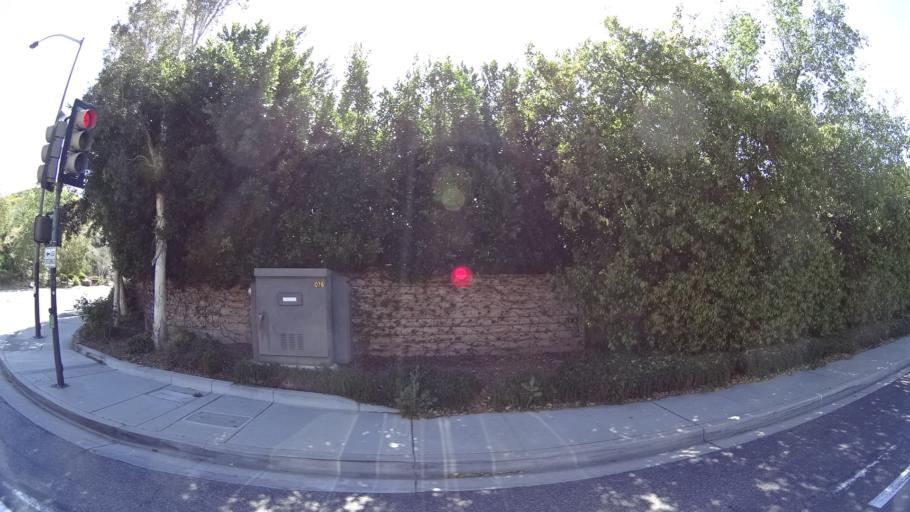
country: US
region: California
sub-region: Ventura County
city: Moorpark
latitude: 34.2323
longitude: -118.8591
